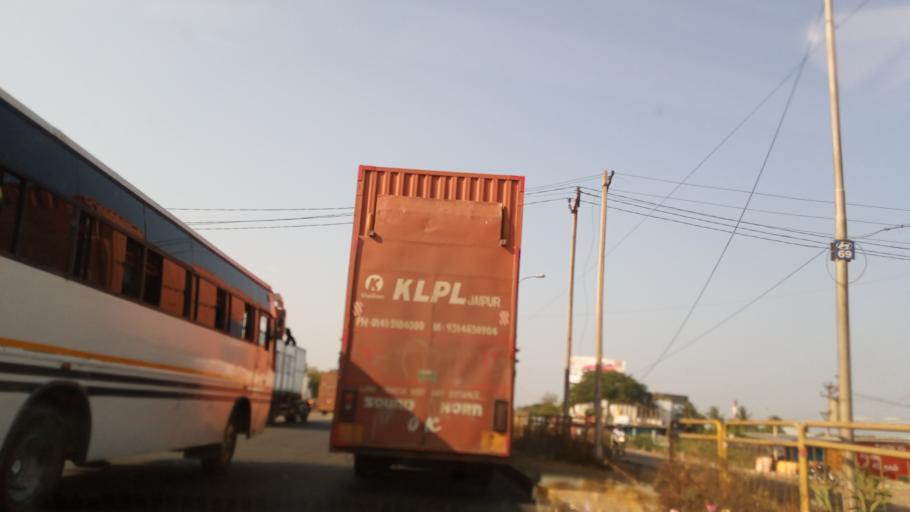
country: IN
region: Tamil Nadu
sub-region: Kancheepuram
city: Sriperumbudur
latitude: 12.9967
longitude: 79.9894
